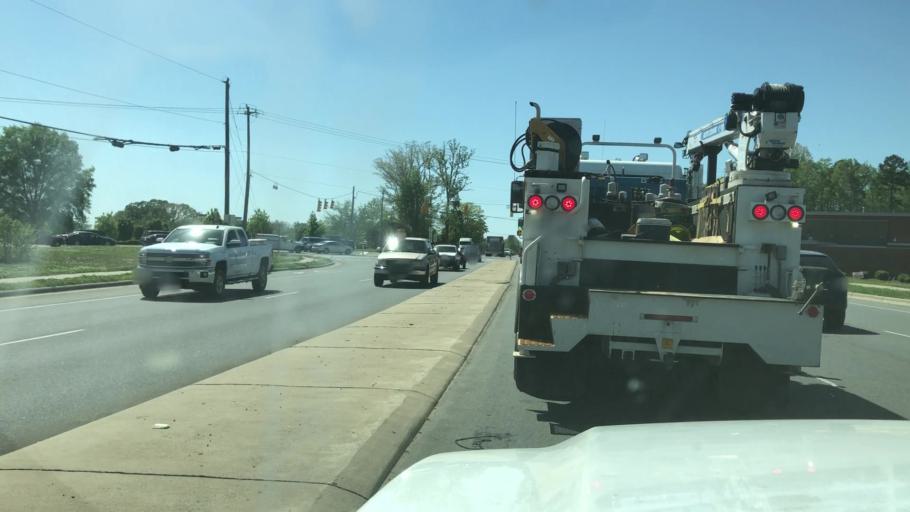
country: US
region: North Carolina
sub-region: Mecklenburg County
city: Huntersville
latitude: 35.3701
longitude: -80.8301
